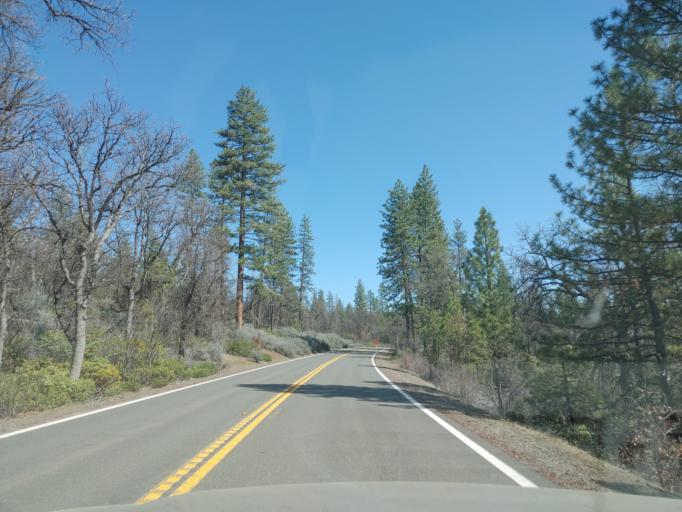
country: US
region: California
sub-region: Shasta County
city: Burney
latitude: 41.0077
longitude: -121.6367
